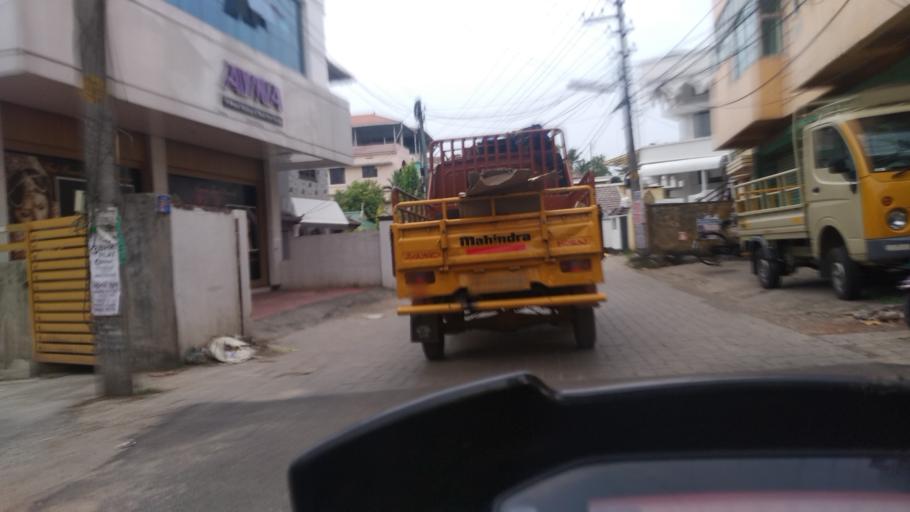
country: IN
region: Kerala
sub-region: Ernakulam
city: Elur
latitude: 10.0148
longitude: 76.3261
